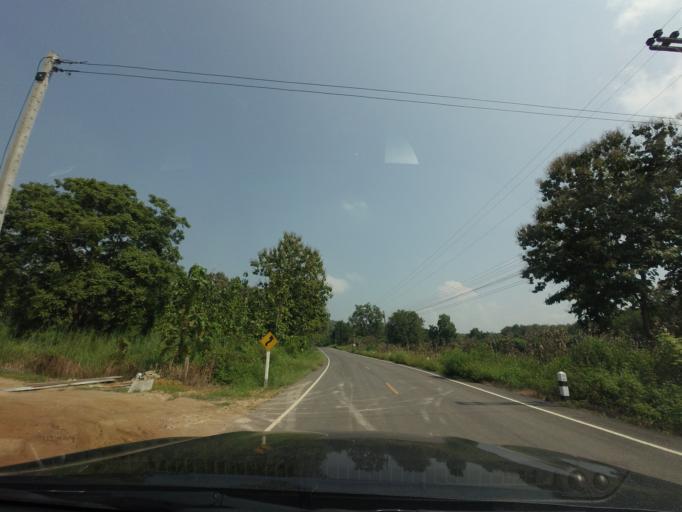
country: TH
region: Nan
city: Nan
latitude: 18.8305
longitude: 100.7744
